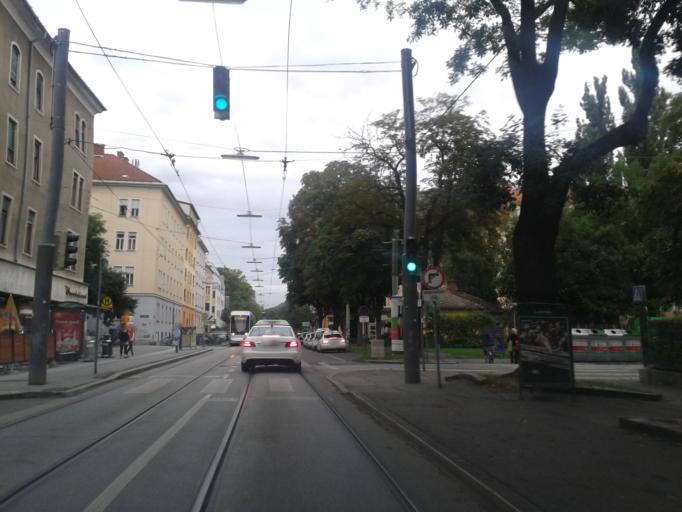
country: AT
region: Styria
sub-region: Graz Stadt
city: Graz
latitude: 47.0823
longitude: 15.4332
